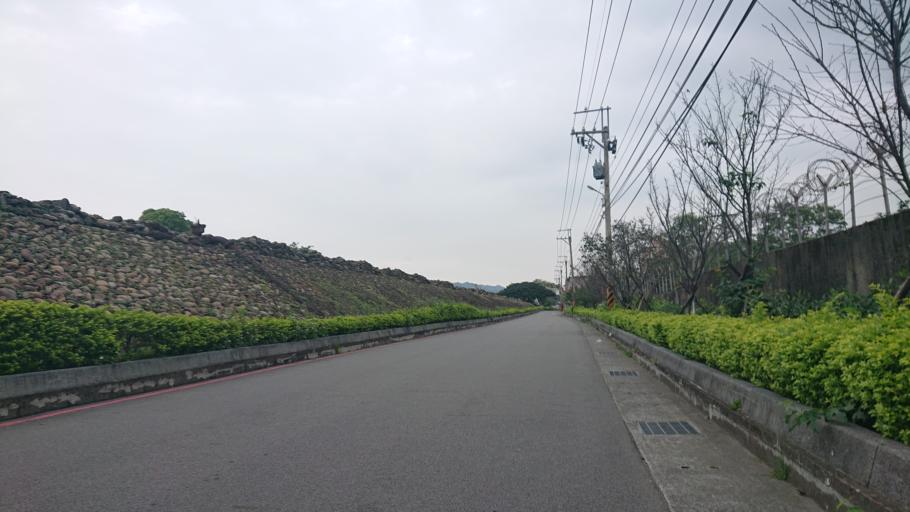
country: TW
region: Taiwan
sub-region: Taoyuan
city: Taoyuan
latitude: 24.9381
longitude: 121.3526
